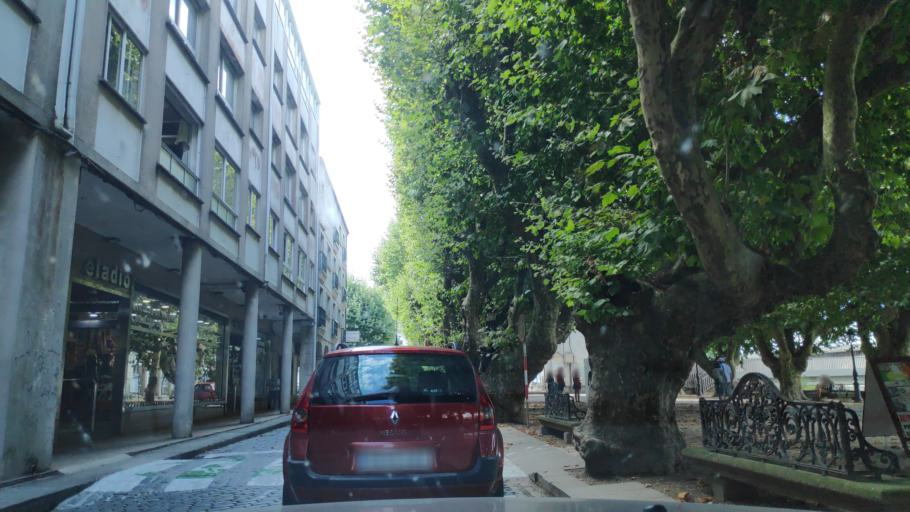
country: ES
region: Galicia
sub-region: Provincia da Coruna
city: Padron
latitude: 42.7373
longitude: -8.6615
